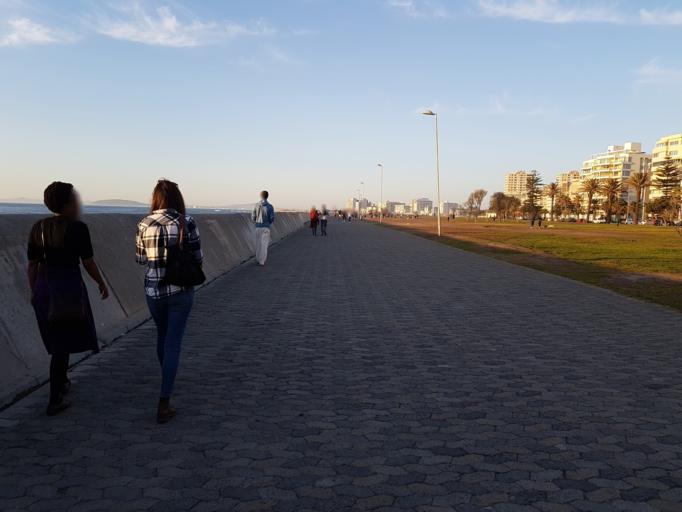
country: ZA
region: Western Cape
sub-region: City of Cape Town
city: Cape Town
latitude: -33.9108
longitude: 18.3890
